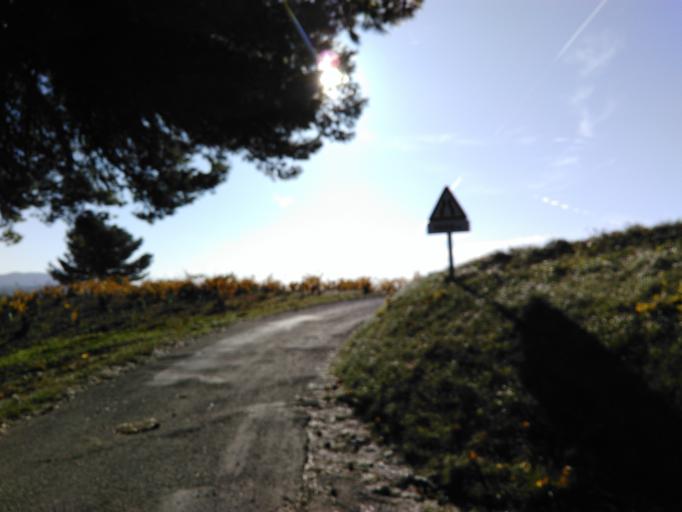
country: FR
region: Provence-Alpes-Cote d'Azur
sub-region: Departement du Vaucluse
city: Sablet
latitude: 44.2433
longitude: 4.9985
